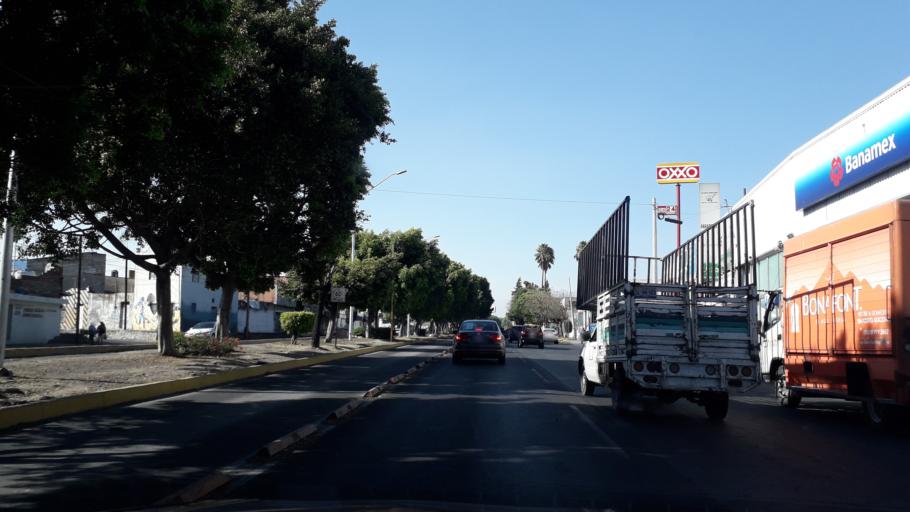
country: MX
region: Puebla
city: Puebla
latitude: 19.0576
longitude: -98.1927
